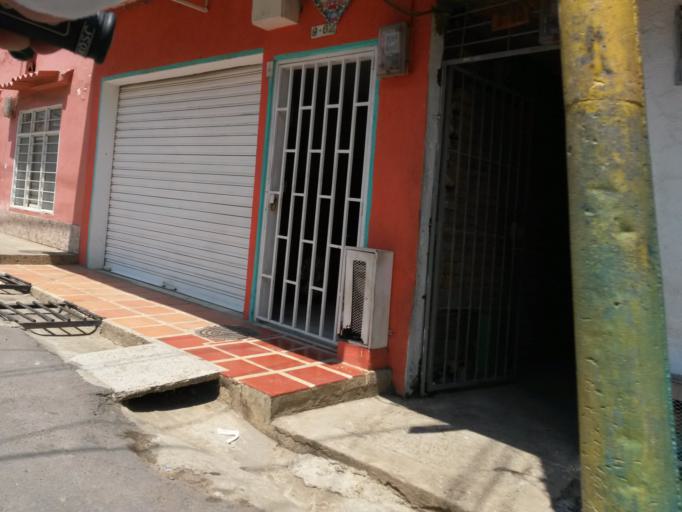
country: CO
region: Cauca
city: Santander de Quilichao
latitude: 3.0114
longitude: -76.4810
